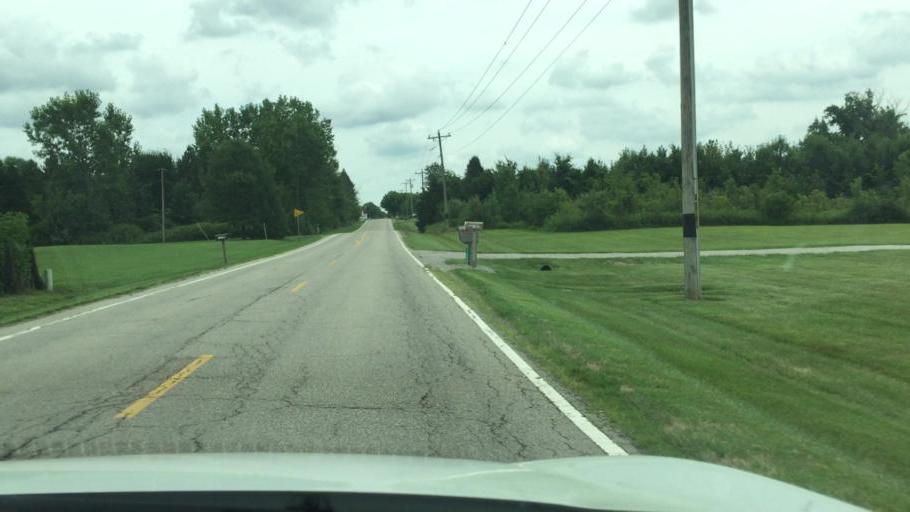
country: US
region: Ohio
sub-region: Champaign County
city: North Lewisburg
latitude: 40.2483
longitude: -83.4827
